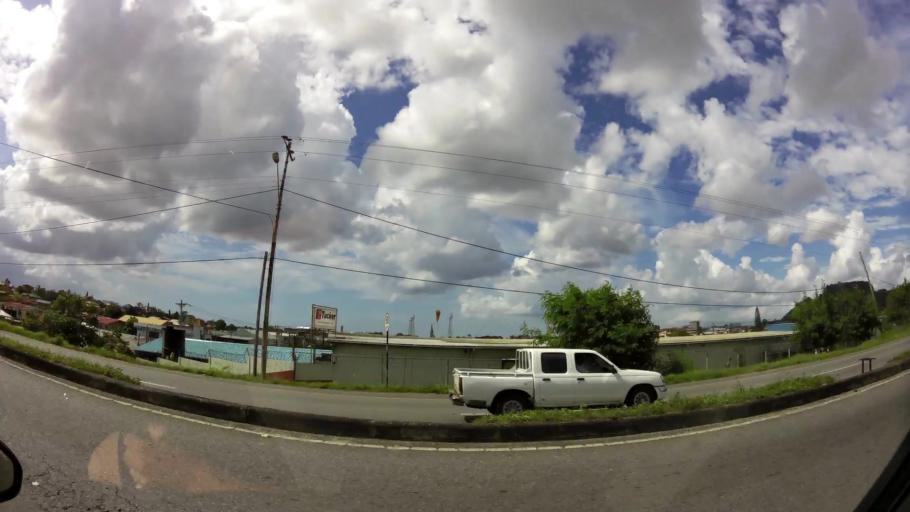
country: TT
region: City of San Fernando
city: Mon Repos
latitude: 10.2640
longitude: -61.4574
